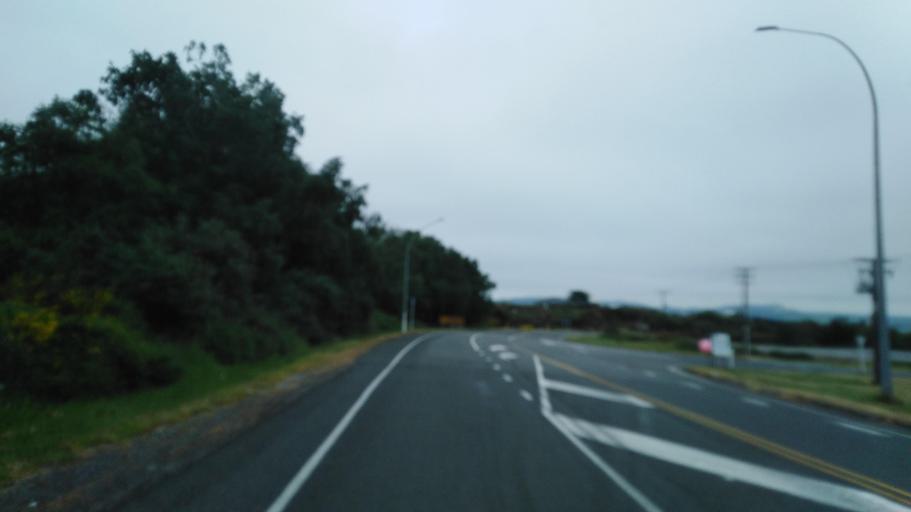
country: NZ
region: Waikato
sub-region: Taupo District
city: Taupo
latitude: -38.7058
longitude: 176.1051
